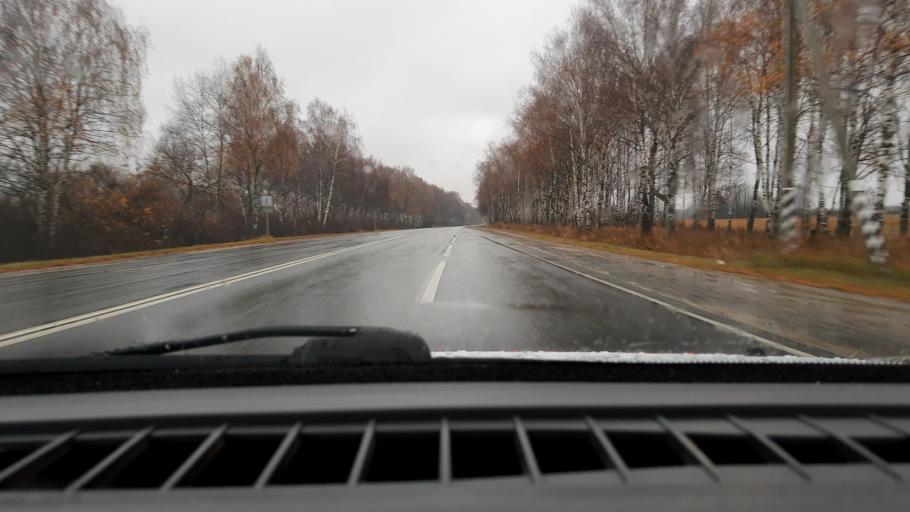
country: RU
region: Nizjnij Novgorod
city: Sitniki
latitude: 56.5081
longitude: 44.0234
